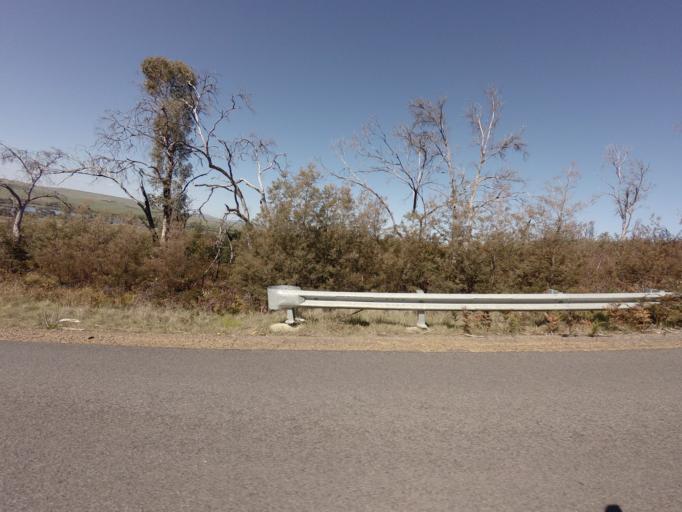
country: AU
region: Tasmania
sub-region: Derwent Valley
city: New Norfolk
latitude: -42.5396
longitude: 146.7209
